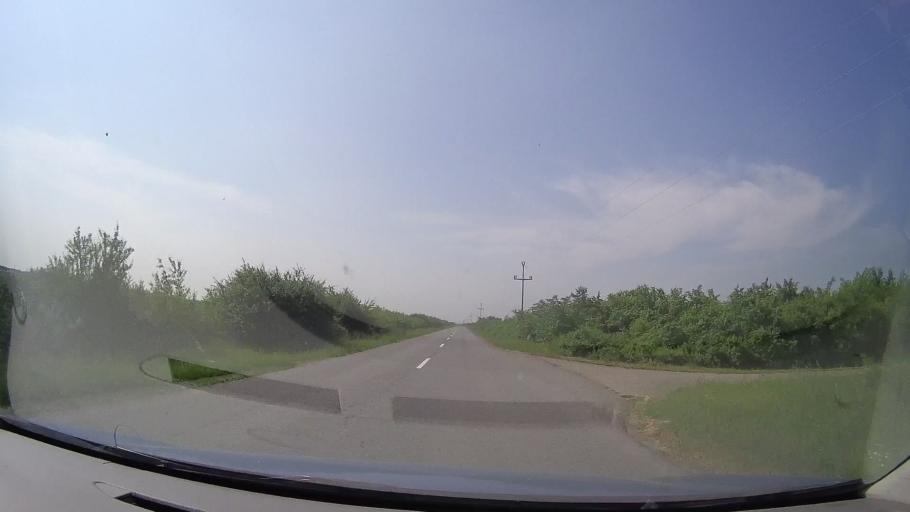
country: RS
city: Jarkovac
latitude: 45.2632
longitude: 20.7640
